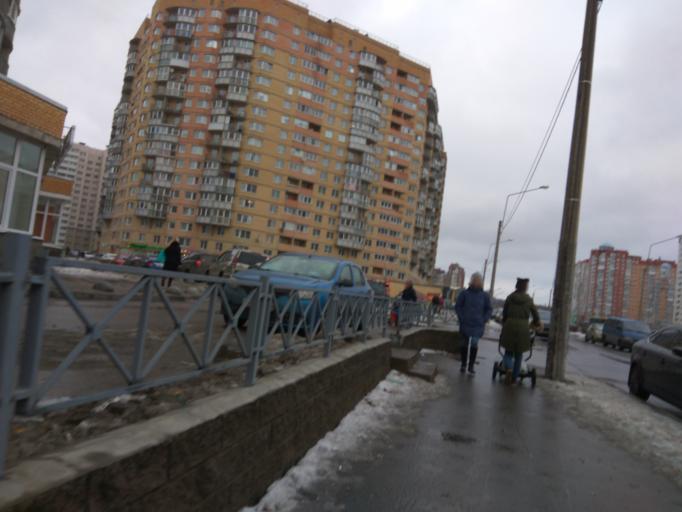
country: RU
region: Leningrad
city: Untolovo
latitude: 60.0031
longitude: 30.2093
